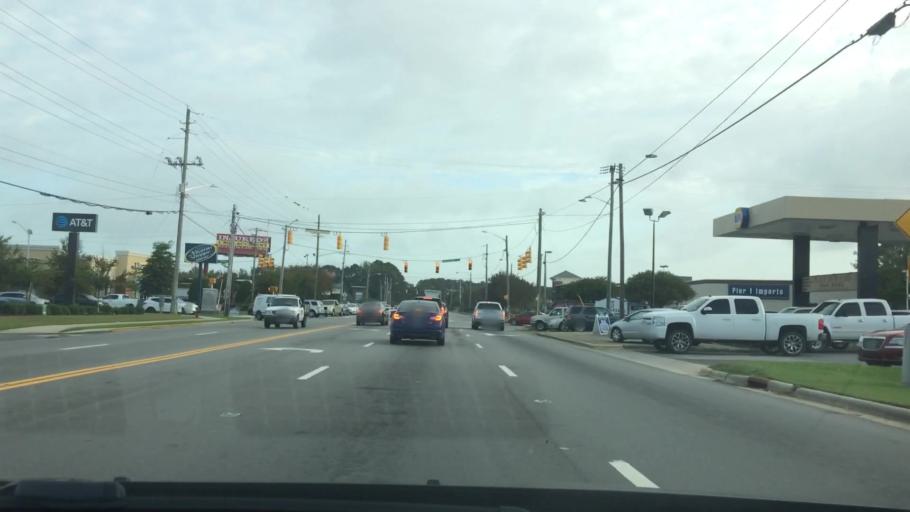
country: US
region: North Carolina
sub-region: Pitt County
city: Greenville
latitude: 35.5851
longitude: -77.3710
